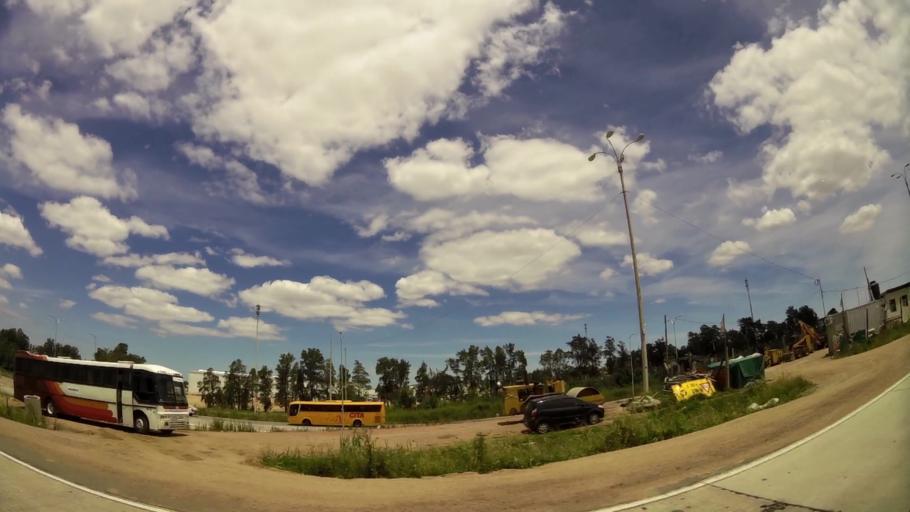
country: UY
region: Montevideo
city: Pajas Blancas
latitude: -34.8525
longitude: -56.2870
